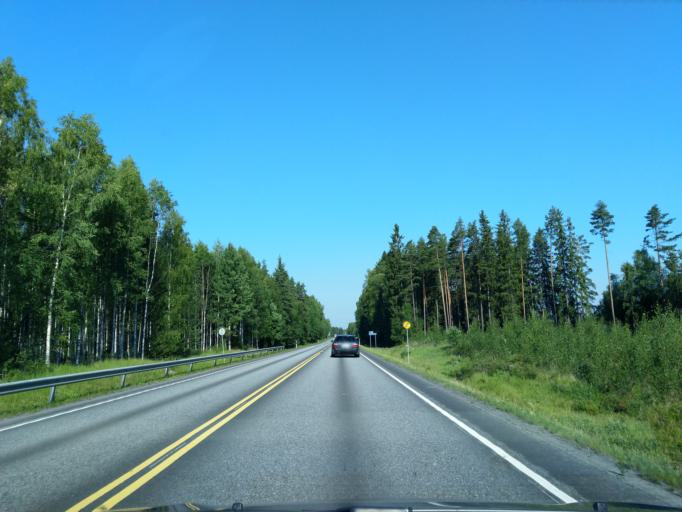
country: FI
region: Satakunta
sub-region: Pori
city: Huittinen
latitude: 61.1406
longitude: 22.7629
